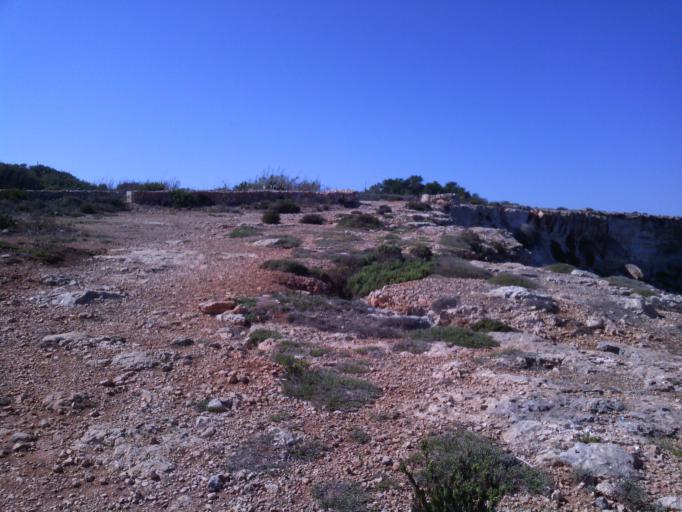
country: MT
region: Il-Mellieha
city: Mellieha
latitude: 35.9824
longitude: 14.3635
